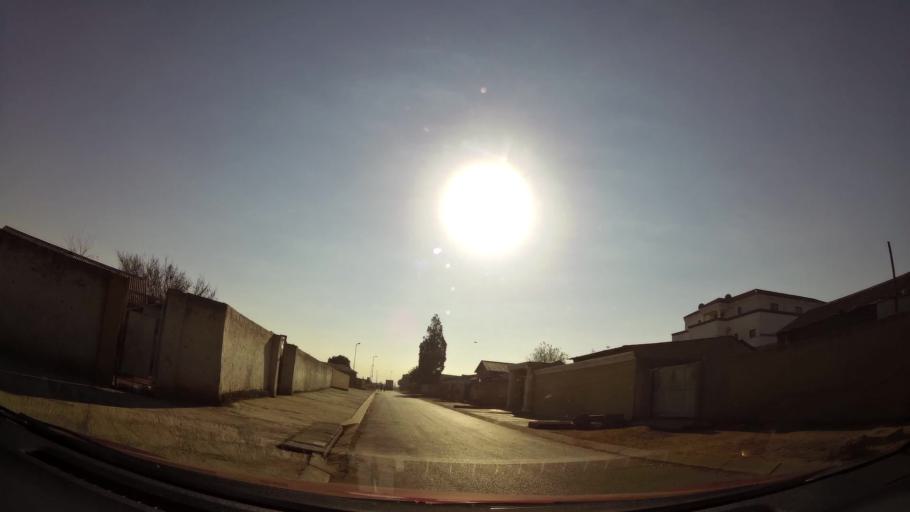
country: ZA
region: Gauteng
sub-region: City of Johannesburg Metropolitan Municipality
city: Soweto
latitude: -26.2311
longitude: 27.9322
